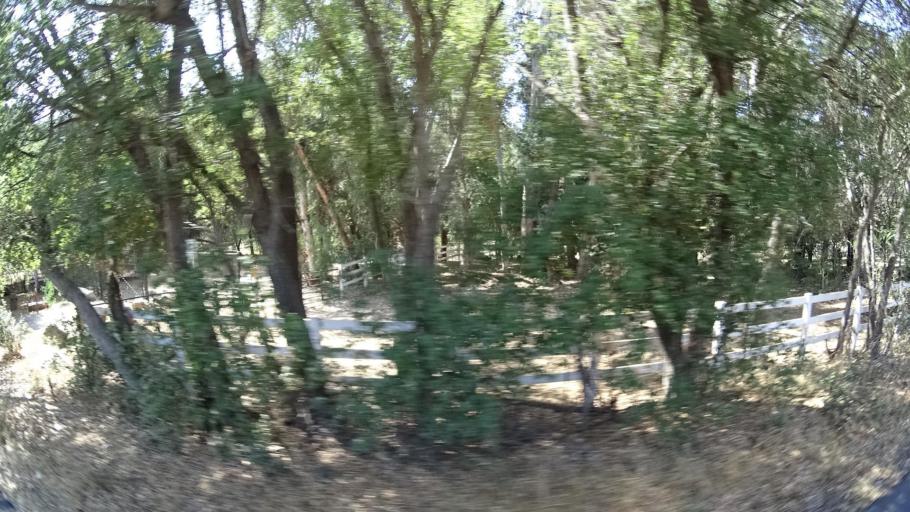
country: US
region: California
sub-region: San Diego County
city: Escondido
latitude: 33.1710
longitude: -117.0998
